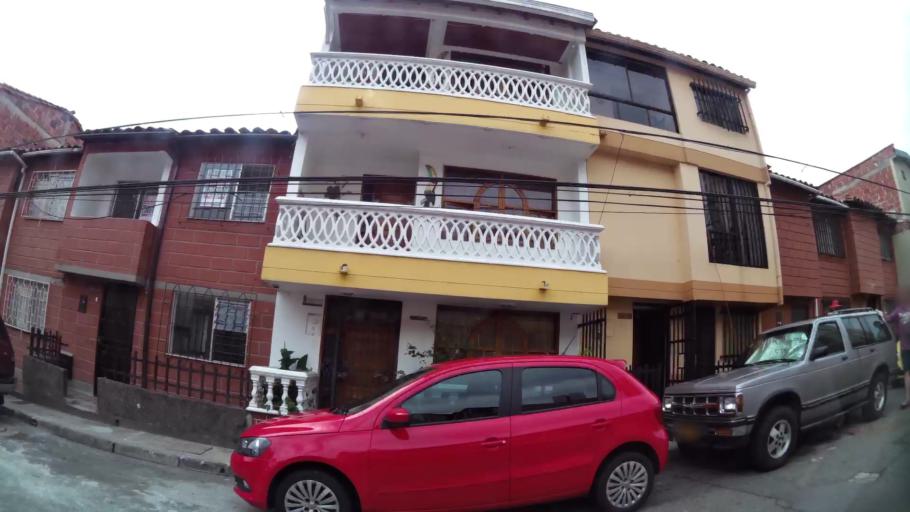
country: CO
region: Antioquia
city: Medellin
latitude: 6.2802
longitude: -75.5988
